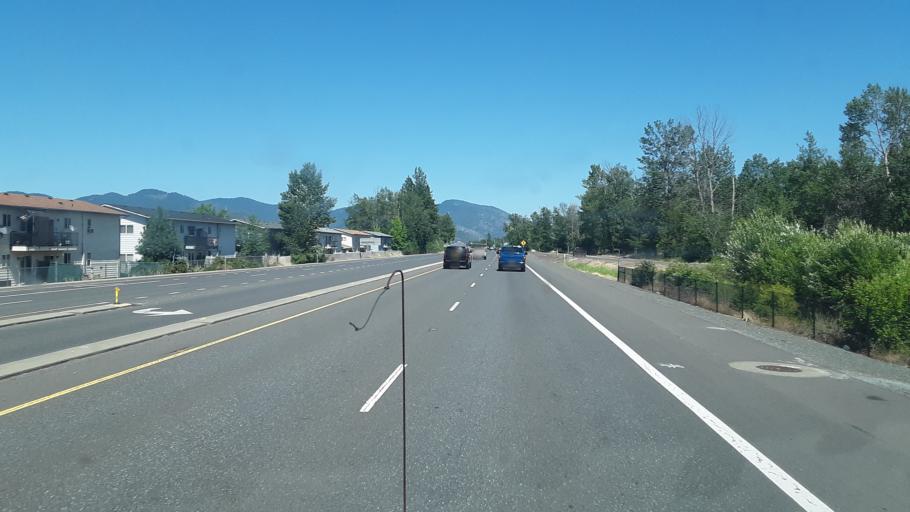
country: US
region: Oregon
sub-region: Josephine County
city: Redwood
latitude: 42.4169
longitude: -123.3761
